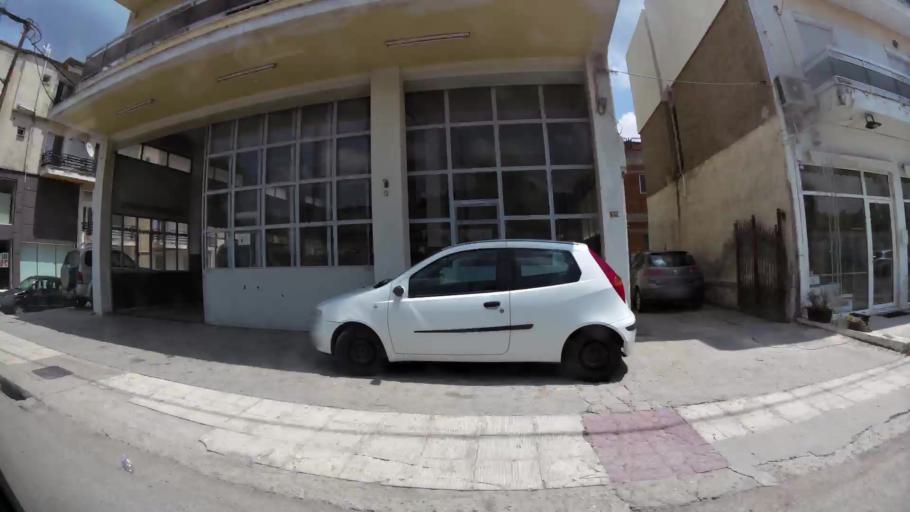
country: GR
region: West Macedonia
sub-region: Nomos Kozanis
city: Kozani
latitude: 40.2936
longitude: 21.7836
